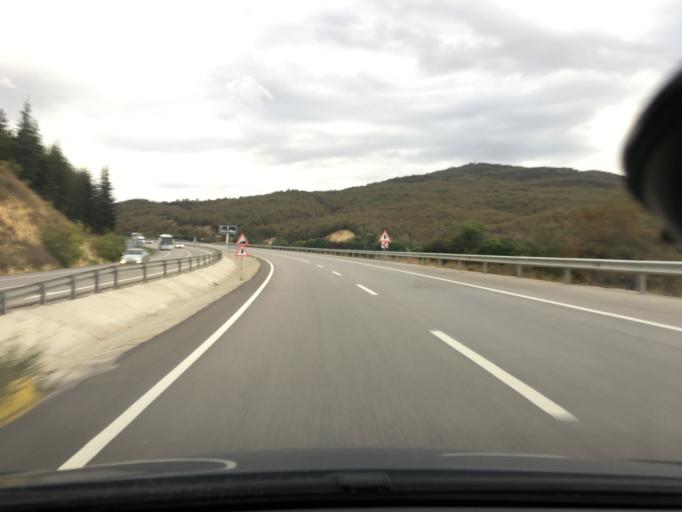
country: TR
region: Afyonkarahisar
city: Sincanli
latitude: 38.7083
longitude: 30.3184
